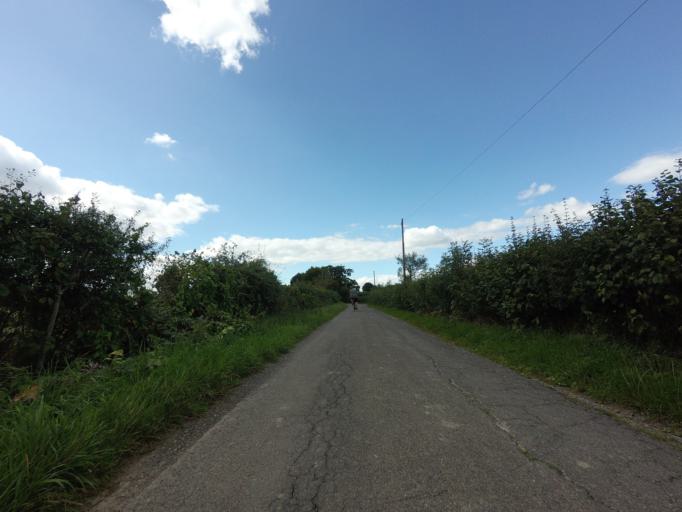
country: GB
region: England
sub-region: Kent
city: Marden
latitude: 51.1509
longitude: 0.4862
